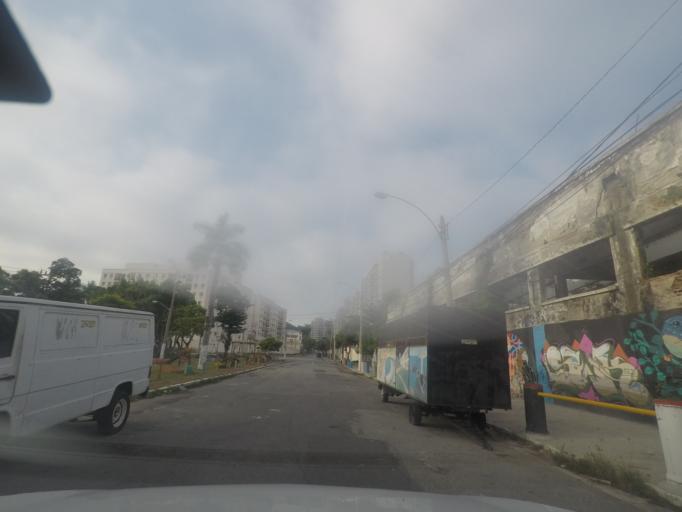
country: BR
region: Rio de Janeiro
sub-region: Duque De Caxias
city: Duque de Caxias
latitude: -22.8364
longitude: -43.2740
